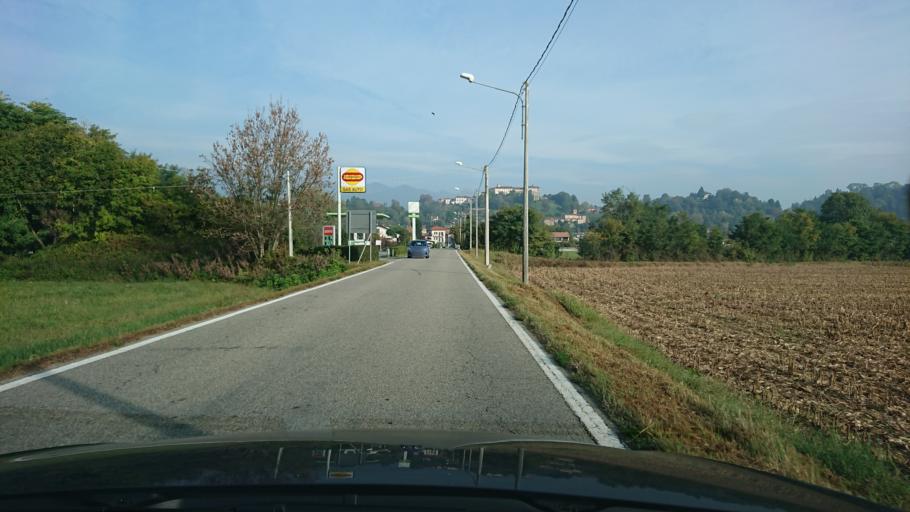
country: IT
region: Piedmont
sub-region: Provincia di Biella
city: Valdengo
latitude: 45.5657
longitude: 8.1316
